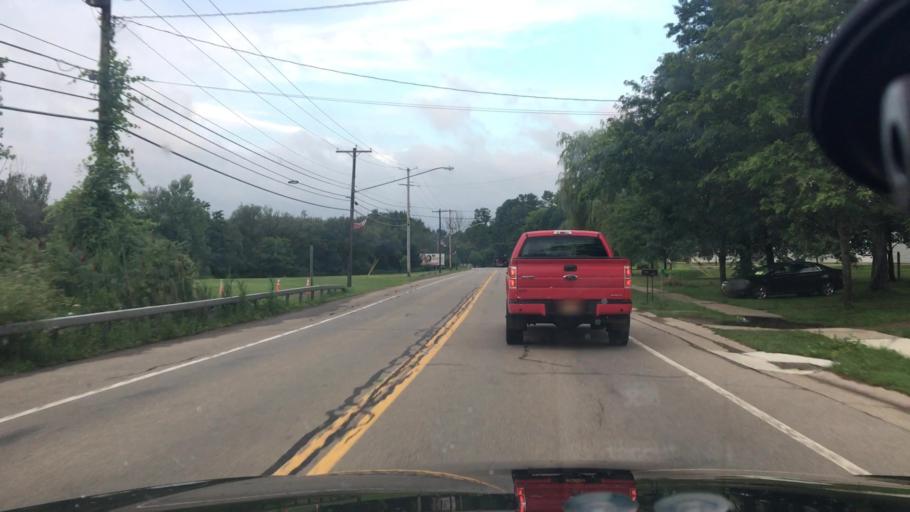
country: US
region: New York
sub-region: Cattaraugus County
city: Randolph
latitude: 42.1695
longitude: -78.9568
